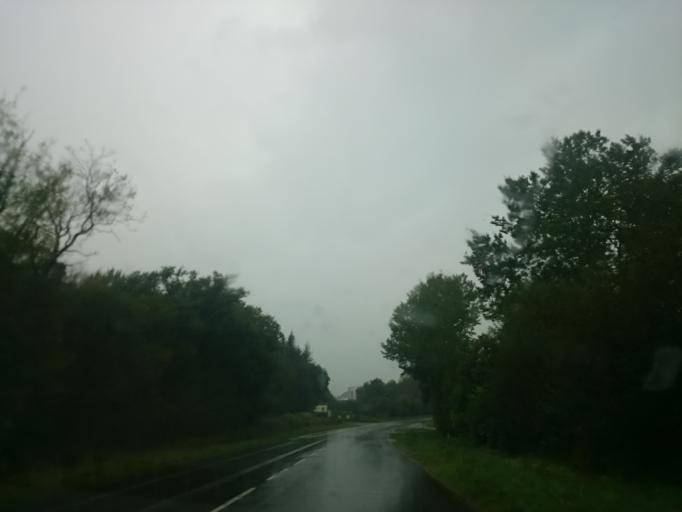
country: FR
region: Brittany
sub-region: Departement du Finistere
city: Plouvien
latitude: 48.5374
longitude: -4.4809
